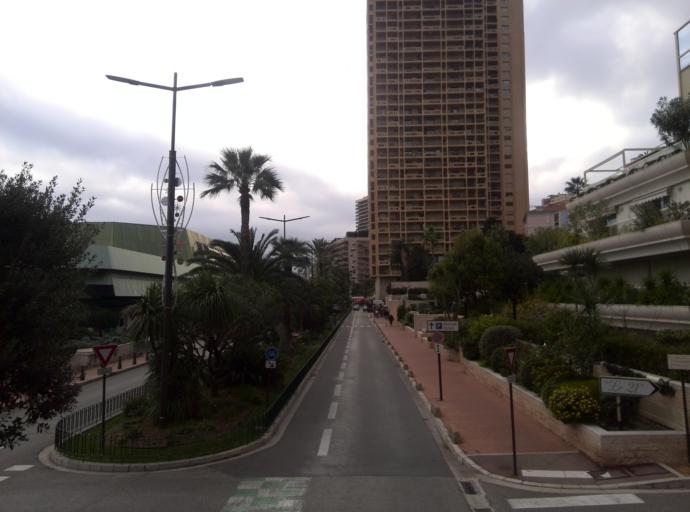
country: MC
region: Commune de Monaco
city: Saint-Roman
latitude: 43.7454
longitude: 7.4318
